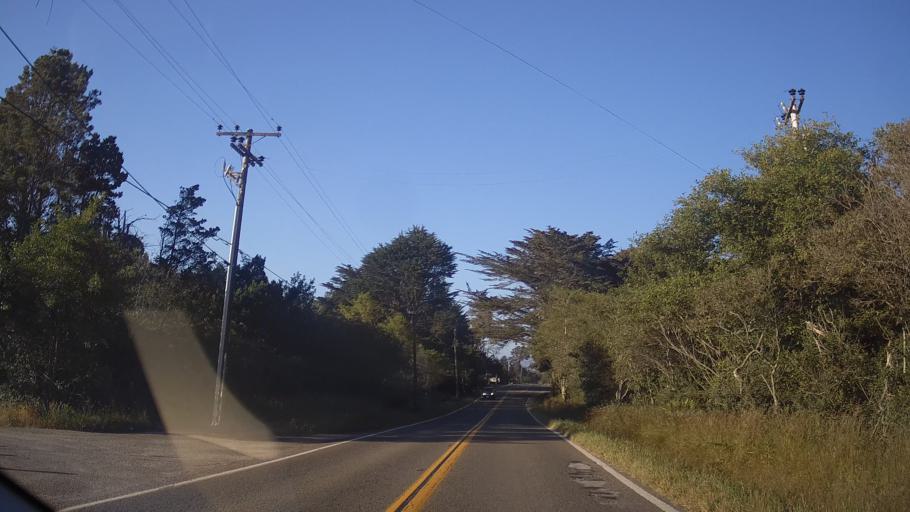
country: US
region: California
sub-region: Mendocino County
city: Fort Bragg
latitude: 39.4794
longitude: -123.7964
